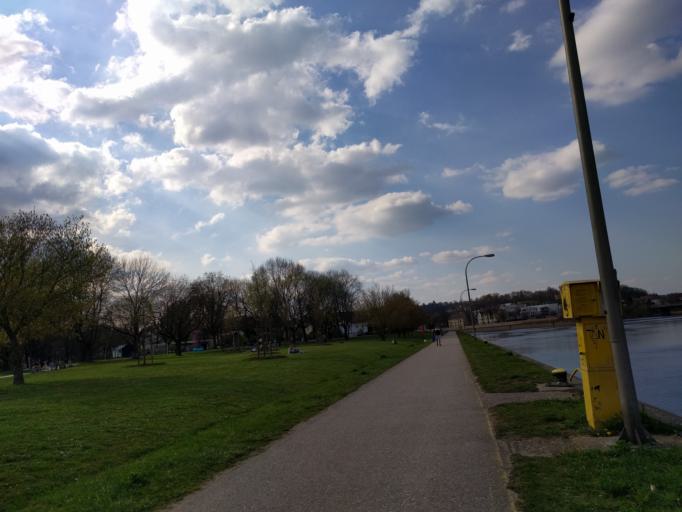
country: DE
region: Bavaria
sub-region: Upper Palatinate
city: Regensburg
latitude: 49.0237
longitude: 12.1059
